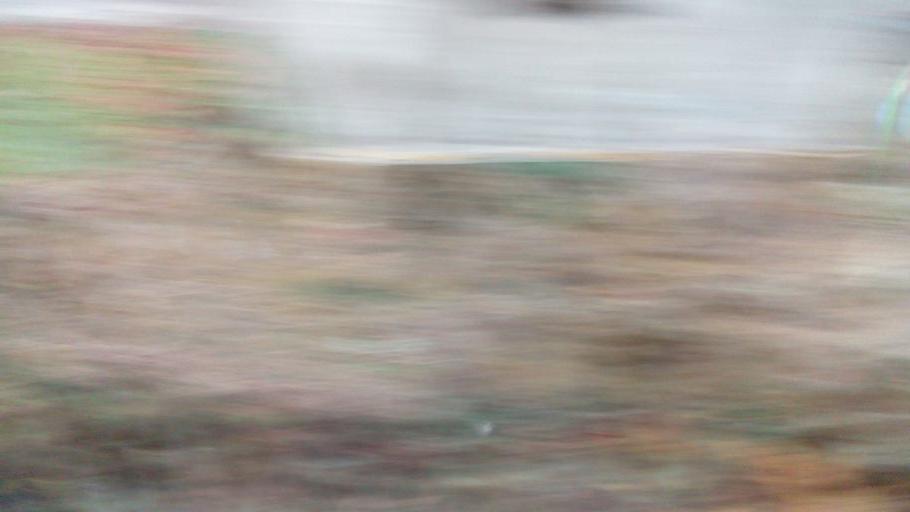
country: TW
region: Taiwan
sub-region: Hualien
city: Hualian
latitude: 24.3710
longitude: 121.3392
